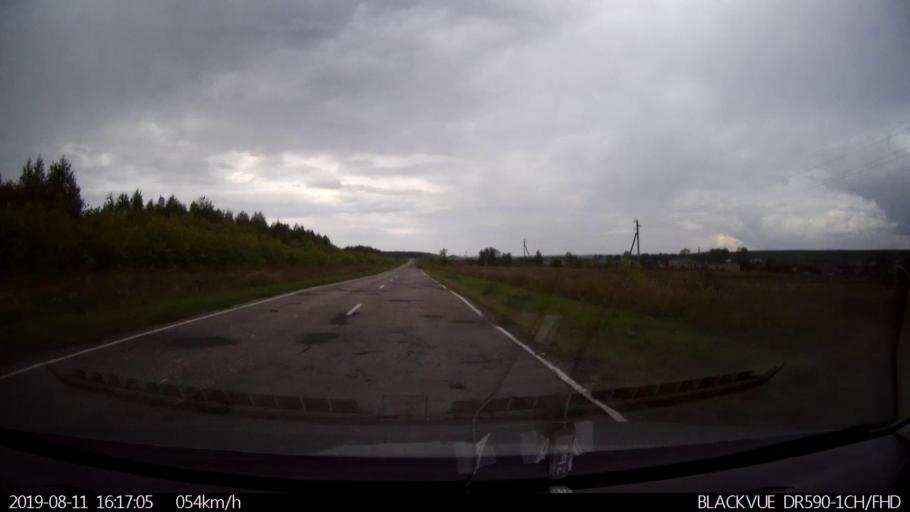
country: RU
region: Ulyanovsk
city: Mayna
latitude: 54.0459
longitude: 47.6179
